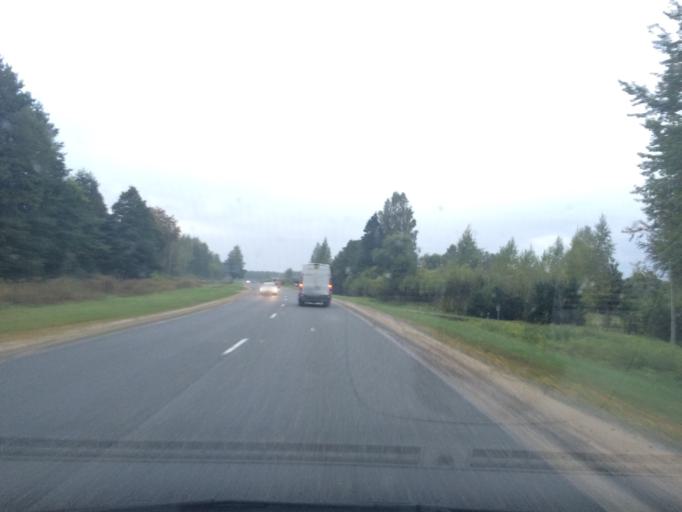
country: LV
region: Plavinu
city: Plavinas
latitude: 56.6172
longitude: 25.7801
